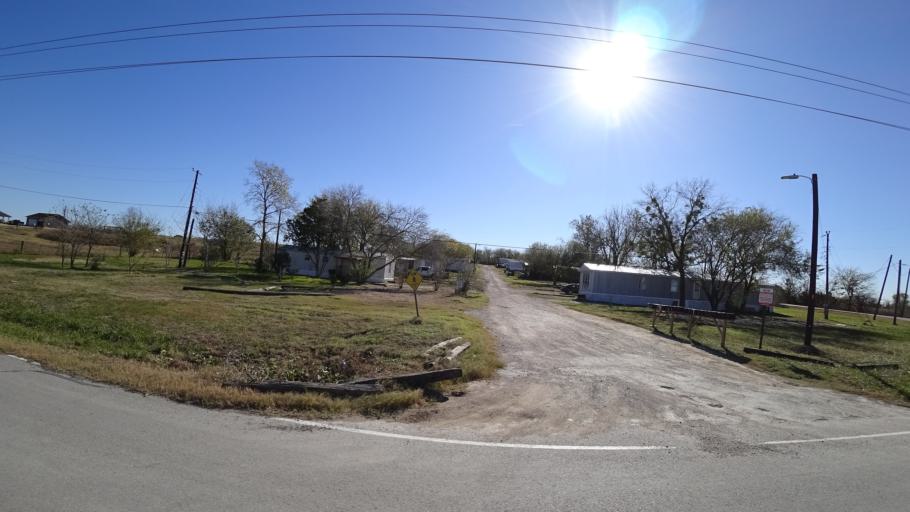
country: US
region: Texas
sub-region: Travis County
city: Onion Creek
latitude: 30.1074
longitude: -97.6739
